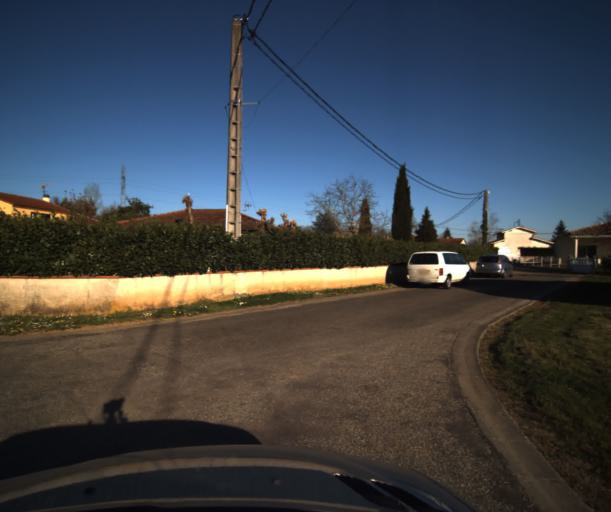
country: FR
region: Midi-Pyrenees
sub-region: Departement du Tarn-et-Garonne
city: Bressols
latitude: 43.9703
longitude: 1.3210
